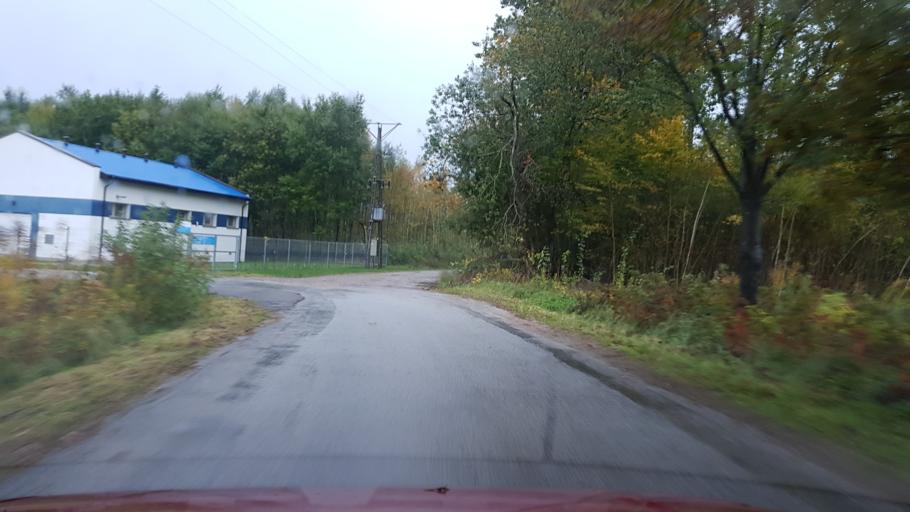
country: PL
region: West Pomeranian Voivodeship
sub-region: Koszalin
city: Koszalin
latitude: 54.1424
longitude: 16.1549
